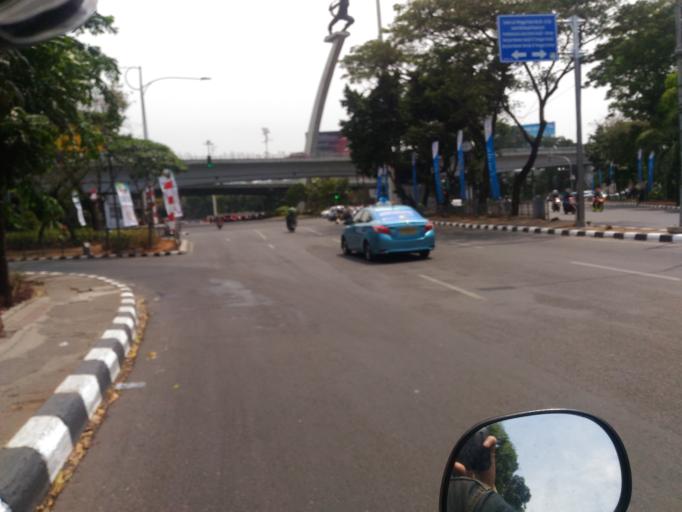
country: ID
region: Jakarta Raya
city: Jakarta
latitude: -6.2423
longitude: 106.8441
